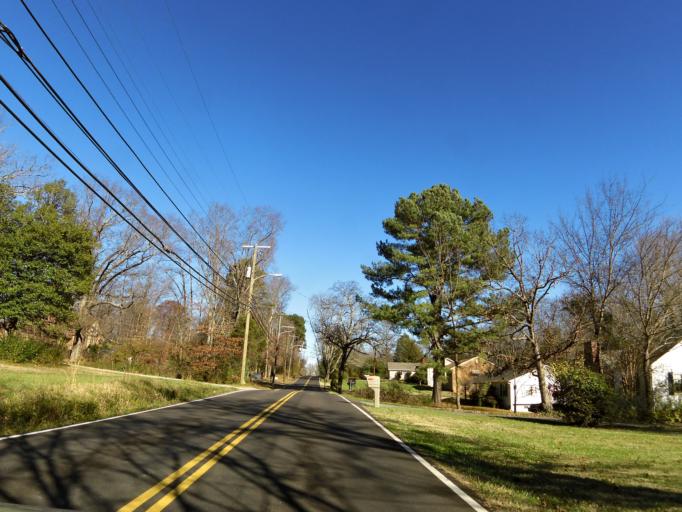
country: US
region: Tennessee
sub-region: Knox County
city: Knoxville
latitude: 36.0238
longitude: -83.9423
